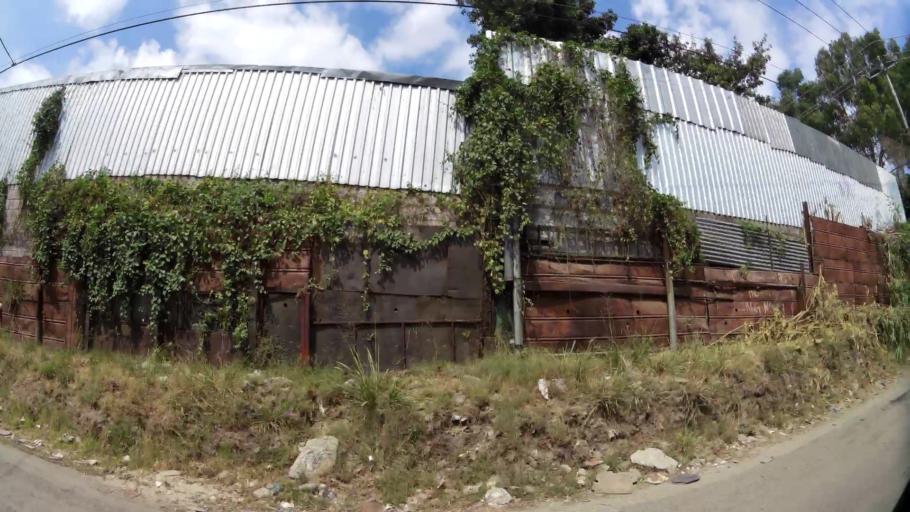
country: SV
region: San Salvador
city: Mejicanos
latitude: 13.7167
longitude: -89.2324
